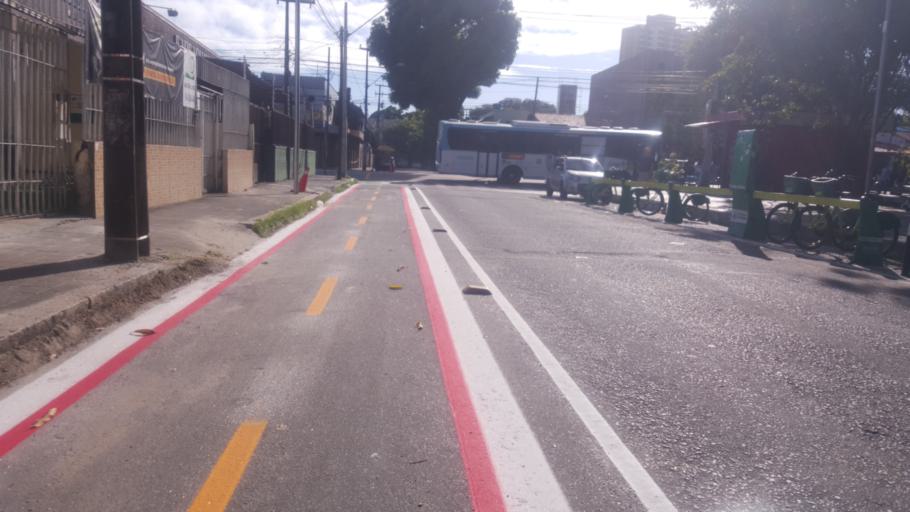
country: BR
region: Ceara
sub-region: Fortaleza
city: Fortaleza
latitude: -3.7425
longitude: -38.5375
